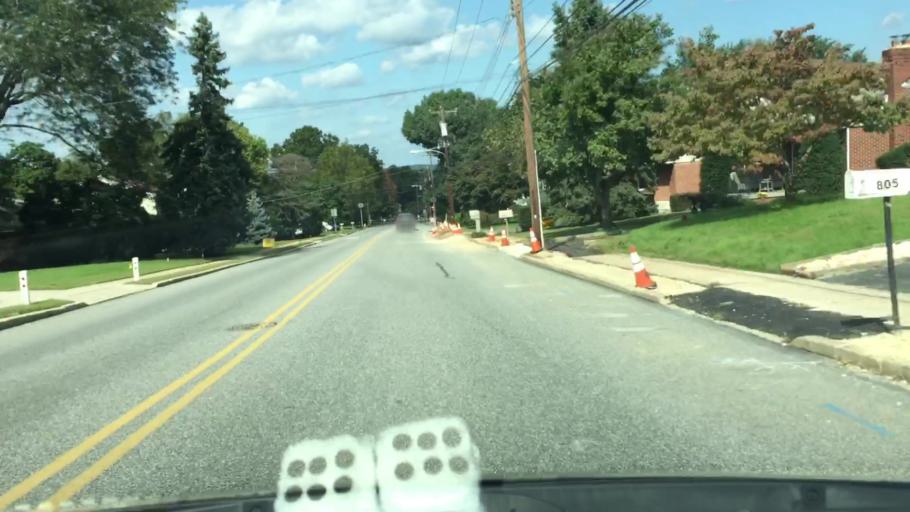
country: US
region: Pennsylvania
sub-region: Montgomery County
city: Norristown
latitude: 40.1228
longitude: -75.3072
